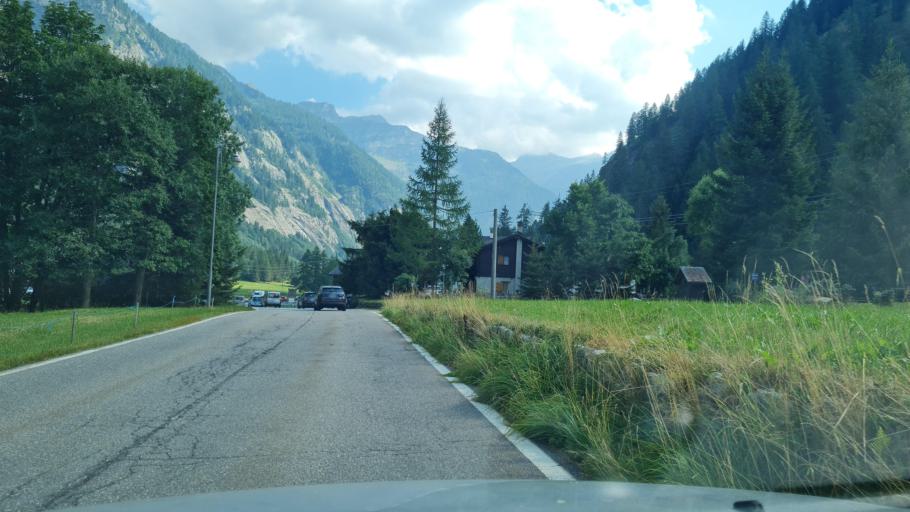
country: IT
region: Piedmont
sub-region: Provincia Verbano-Cusio-Ossola
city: Formazza
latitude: 46.3687
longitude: 8.4286
